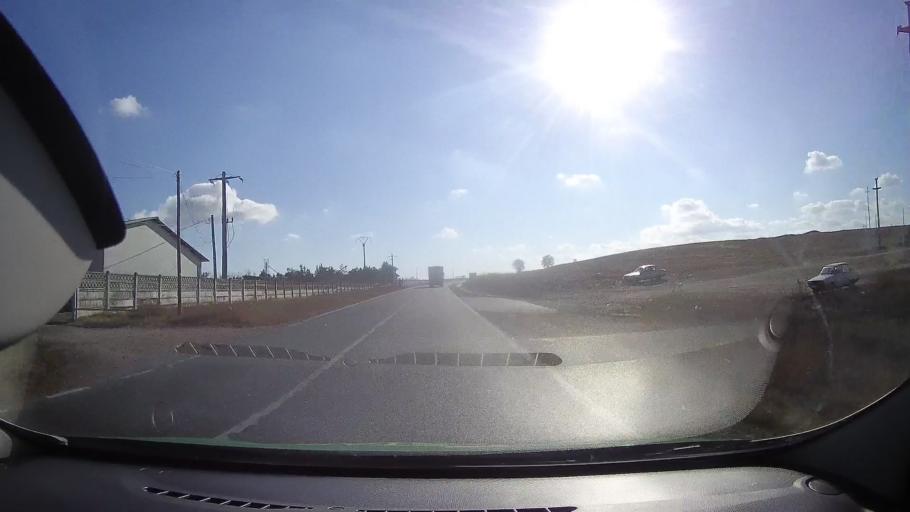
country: RO
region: Tulcea
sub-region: Comuna Baia
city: Baia
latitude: 44.7170
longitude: 28.6812
